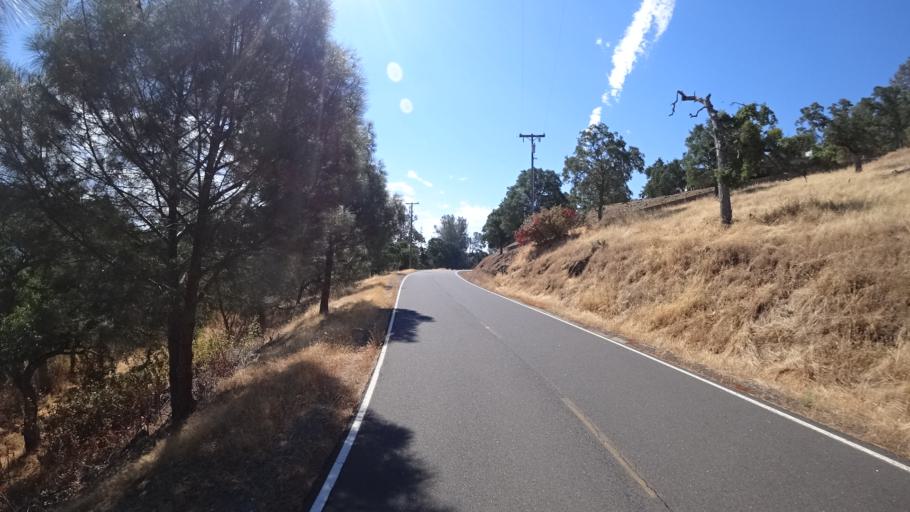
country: US
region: California
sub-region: Calaveras County
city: Copperopolis
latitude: 37.9316
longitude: -120.6319
